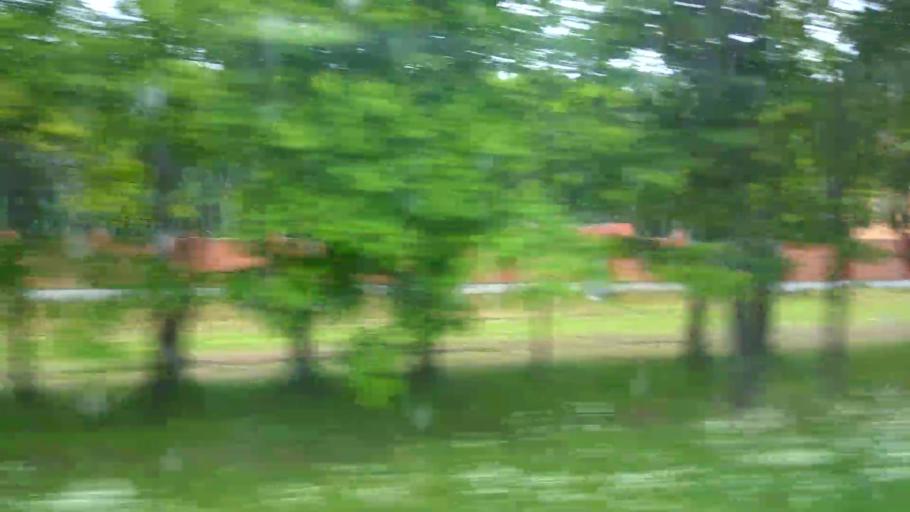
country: RU
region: Moskovskaya
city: Ozherel'ye
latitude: 54.8328
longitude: 38.2815
